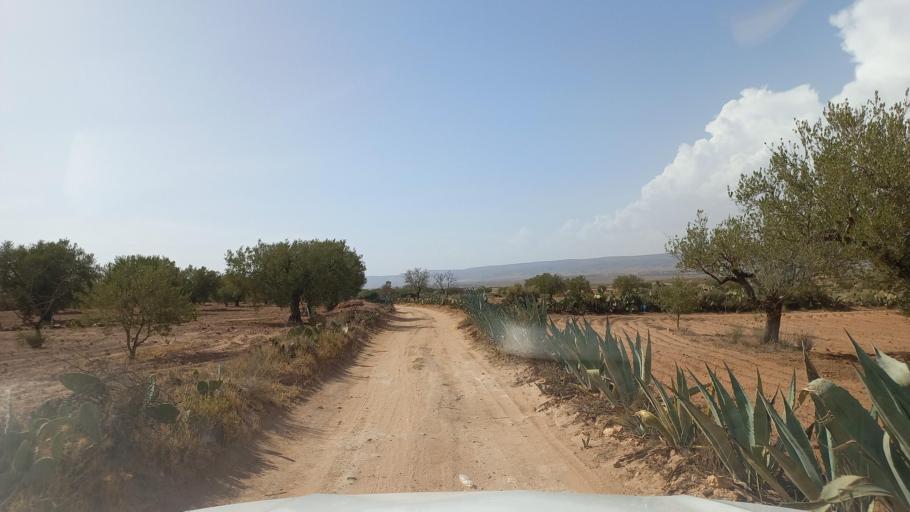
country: TN
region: Al Qasrayn
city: Kasserine
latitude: 35.2106
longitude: 8.9809
